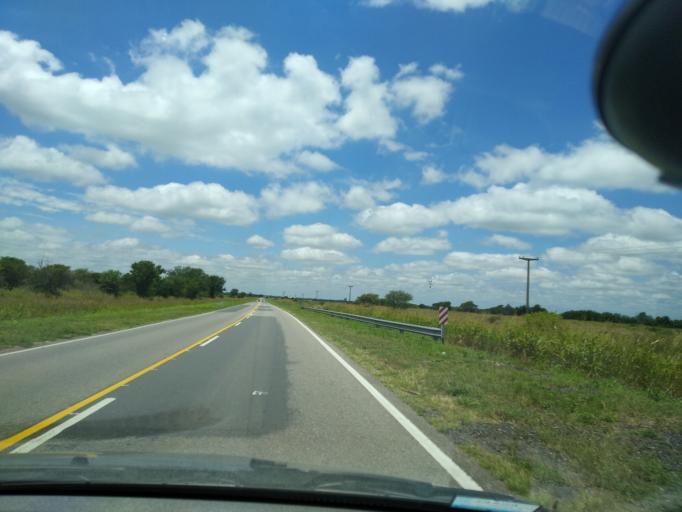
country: AR
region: Cordoba
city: Alta Gracia
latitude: -31.6542
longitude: -64.2763
